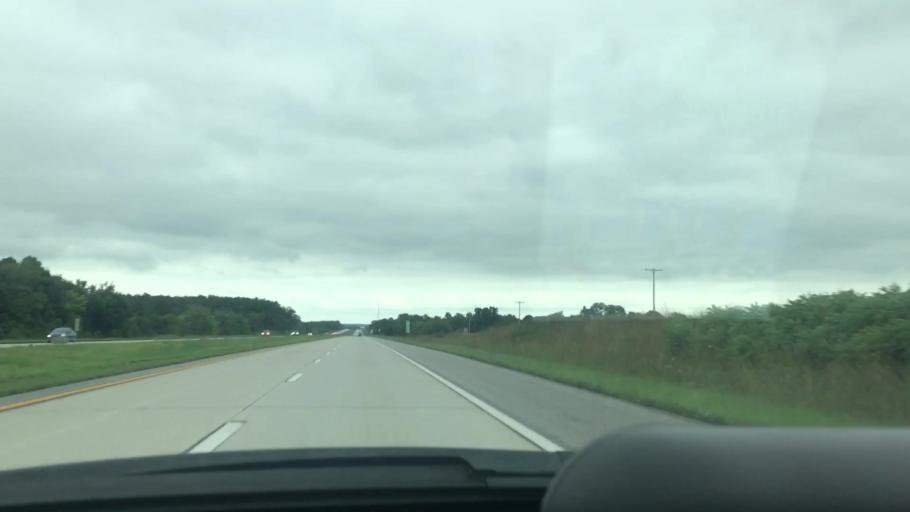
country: US
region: Missouri
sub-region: Greene County
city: Fair Grove
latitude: 37.4850
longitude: -93.1392
